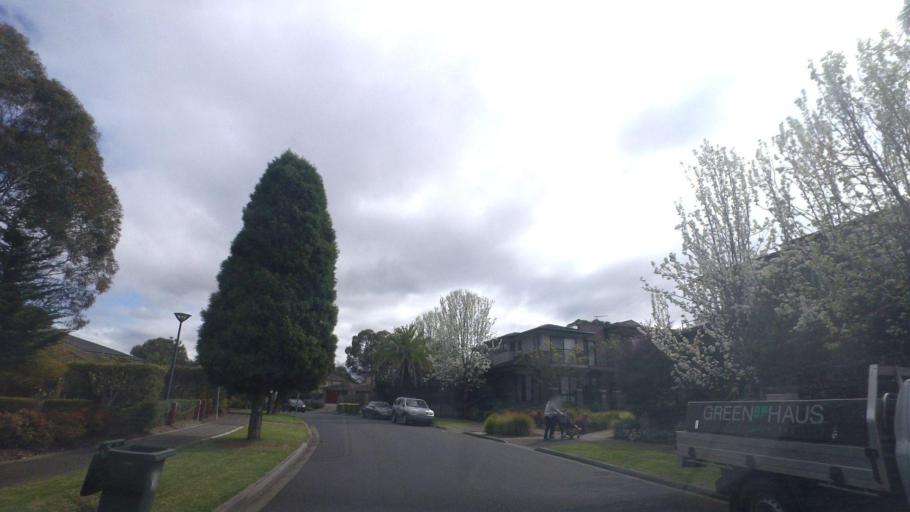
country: AU
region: Victoria
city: Macleod
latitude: -37.7159
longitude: 145.0625
